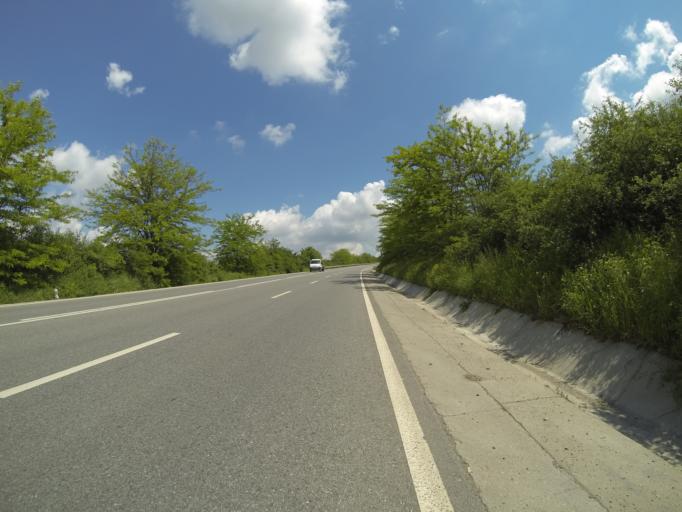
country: RO
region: Dolj
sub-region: Comuna Carcea
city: Carcea
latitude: 44.2660
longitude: 23.8899
